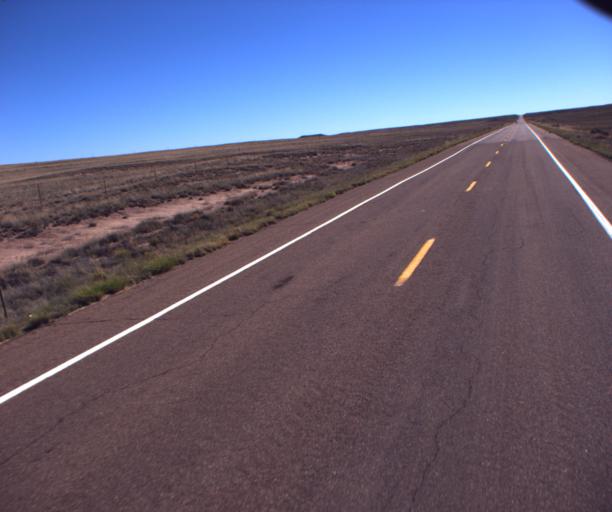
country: US
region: Arizona
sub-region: Navajo County
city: Holbrook
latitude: 34.7850
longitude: -109.8670
